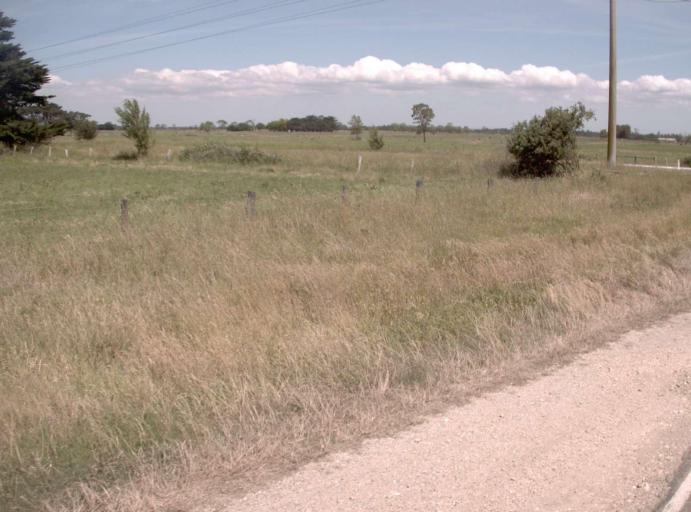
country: AU
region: Victoria
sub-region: Wellington
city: Heyfield
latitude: -37.9908
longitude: 146.8863
